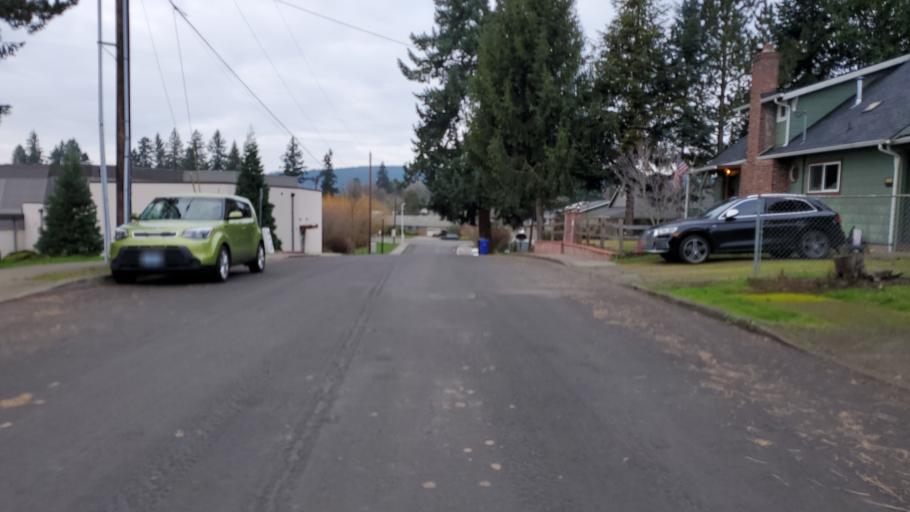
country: US
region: Oregon
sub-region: Clackamas County
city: Gladstone
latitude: 45.3883
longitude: -122.5979
